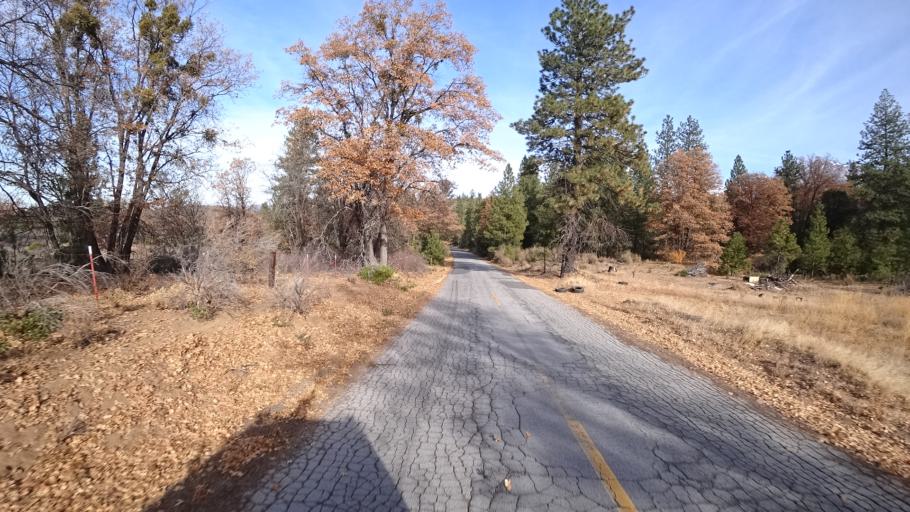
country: US
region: California
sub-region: Siskiyou County
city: Weed
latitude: 41.4450
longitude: -122.3829
